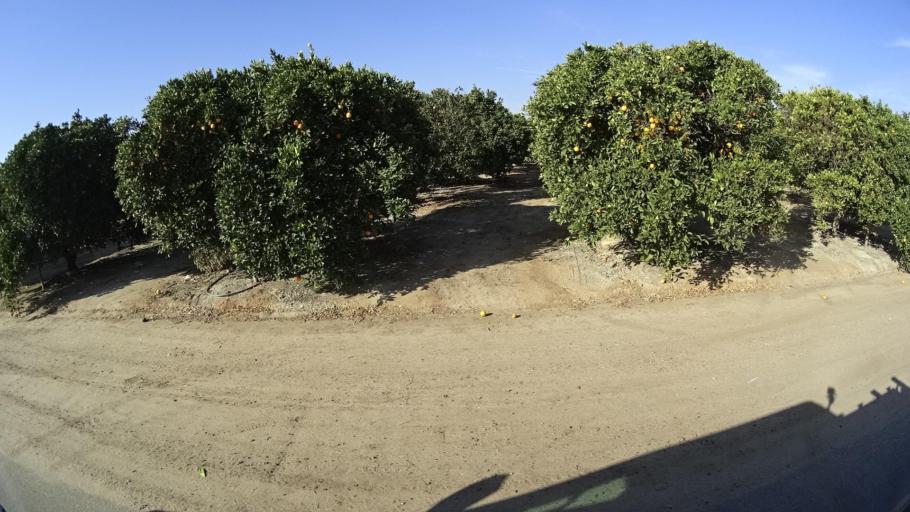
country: US
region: California
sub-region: Kern County
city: Lamont
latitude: 35.3536
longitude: -118.8963
